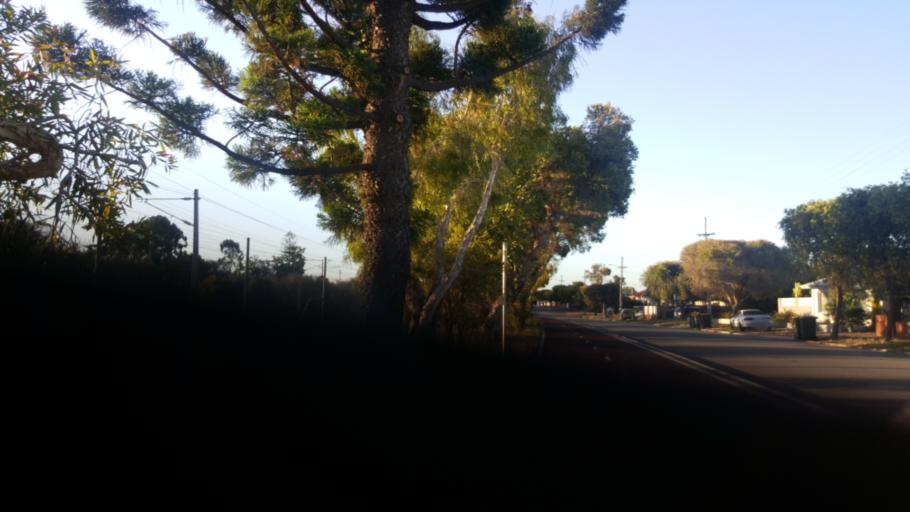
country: AU
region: Western Australia
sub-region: Victoria Park
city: East Victoria Park
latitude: -31.9850
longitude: 115.9150
